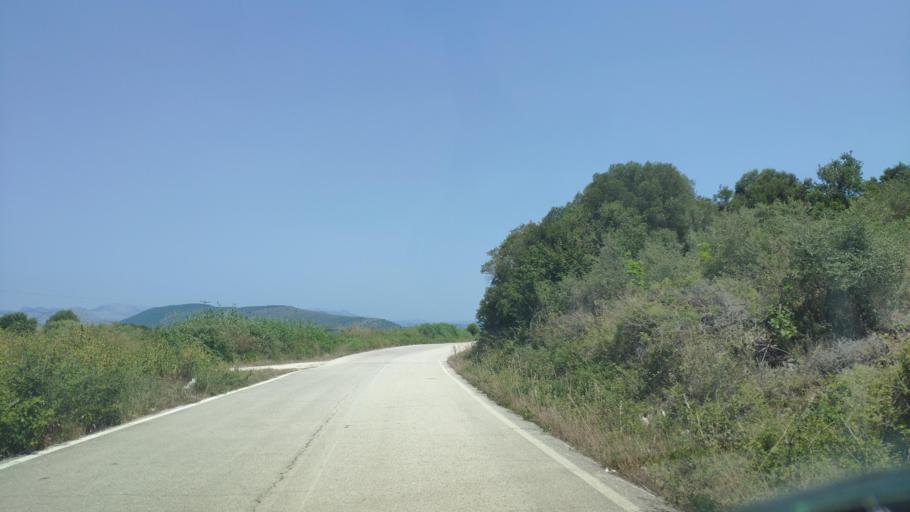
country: GR
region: Epirus
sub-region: Nomos Artas
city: Aneza
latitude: 39.0394
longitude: 20.8595
